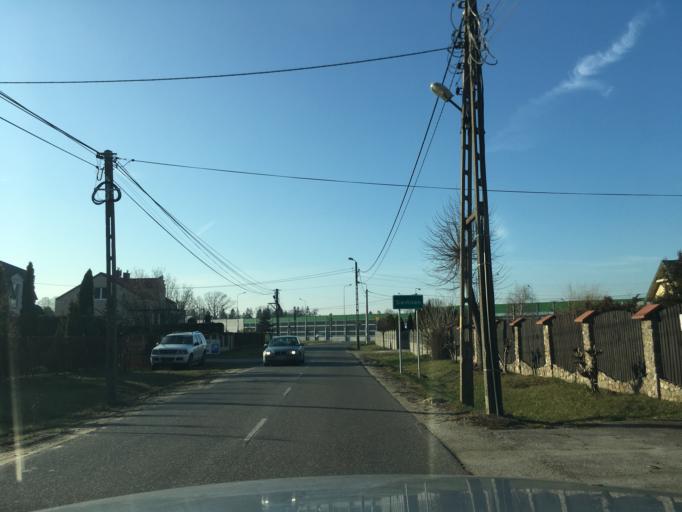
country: PL
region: Lodz Voivodeship
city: Zabia Wola
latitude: 52.0537
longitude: 20.7258
